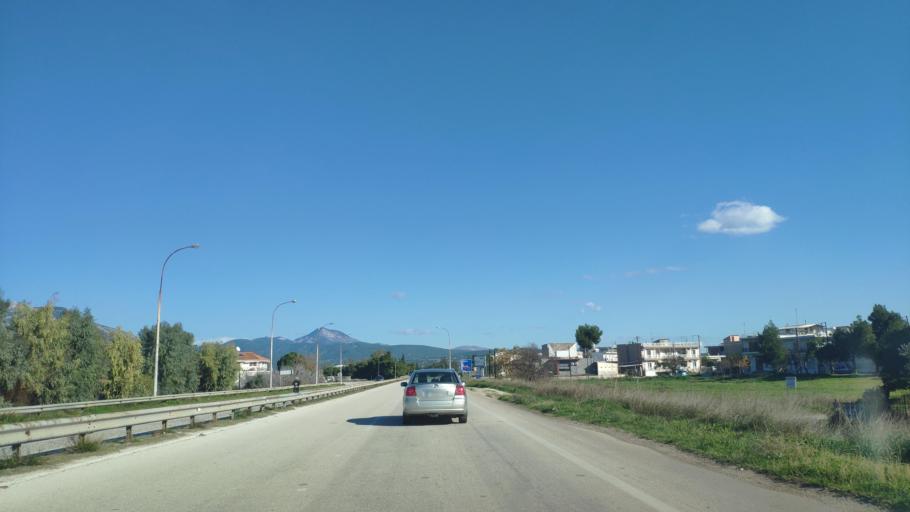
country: GR
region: Peloponnese
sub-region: Nomos Korinthias
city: Korinthos
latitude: 37.9357
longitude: 22.9500
